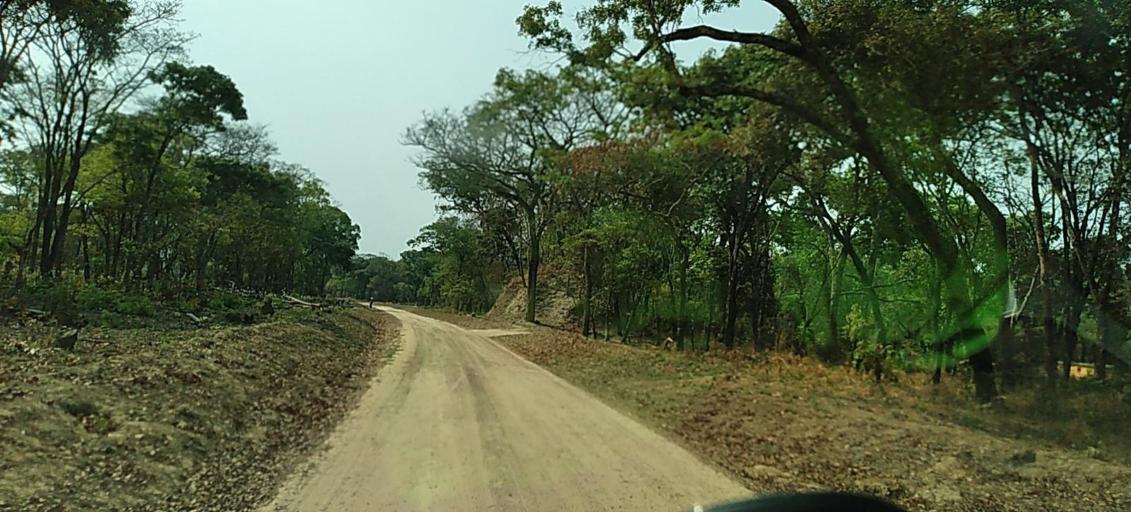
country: ZM
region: North-Western
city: Solwezi
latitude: -12.7029
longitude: 26.4152
